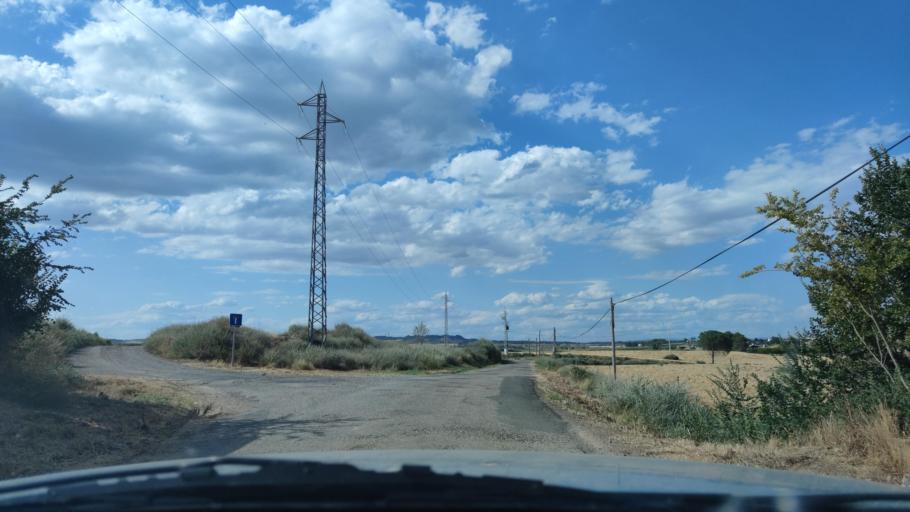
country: ES
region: Catalonia
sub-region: Provincia de Lleida
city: Alcarras
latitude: 41.5879
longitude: 0.5325
